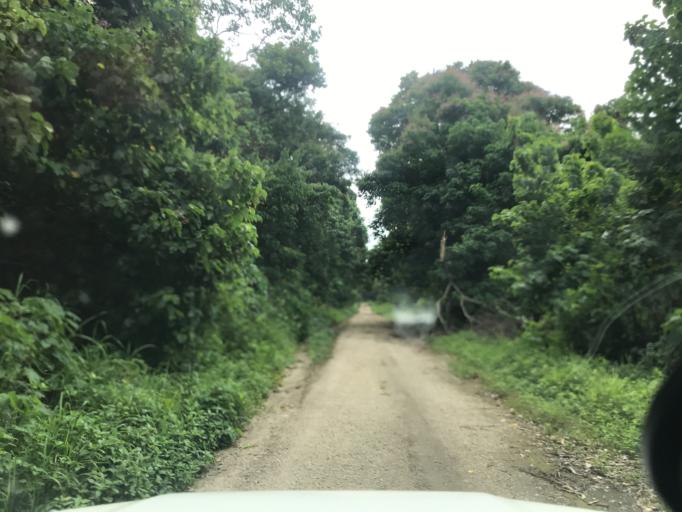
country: VU
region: Sanma
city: Port-Olry
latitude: -15.1698
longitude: 166.9497
